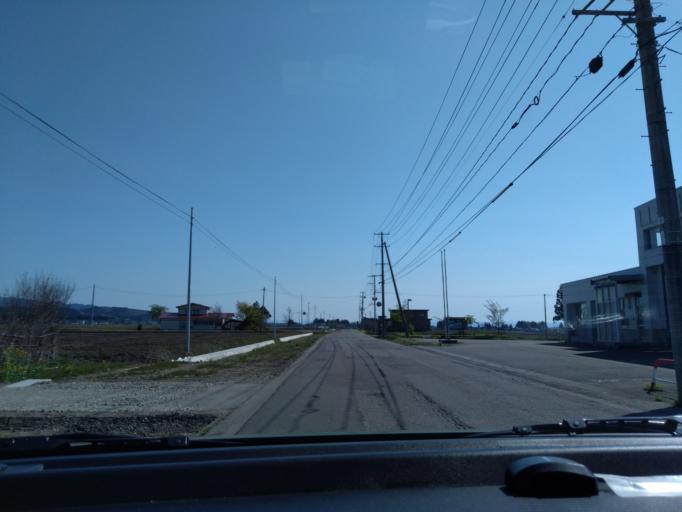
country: JP
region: Akita
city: Kakunodatemachi
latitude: 39.4840
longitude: 140.5906
